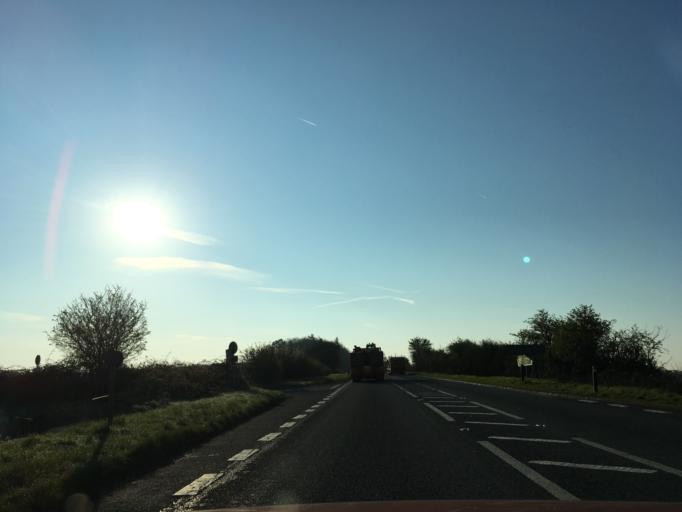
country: GB
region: England
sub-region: Gloucestershire
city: Bourton on the Water
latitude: 51.8103
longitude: -1.7238
